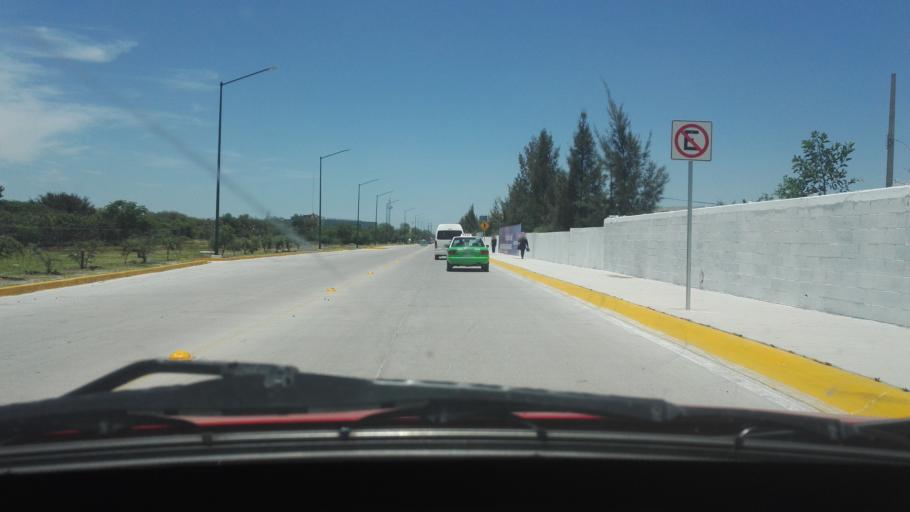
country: MX
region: Guanajuato
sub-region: Leon
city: Ladrilleras del Refugio
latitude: 21.0593
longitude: -101.5688
